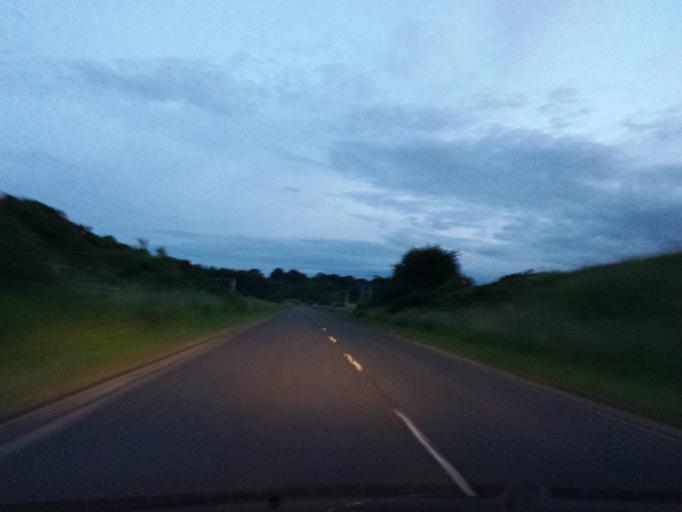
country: GB
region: Scotland
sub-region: The Scottish Borders
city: Duns
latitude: 55.7502
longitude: -2.4069
